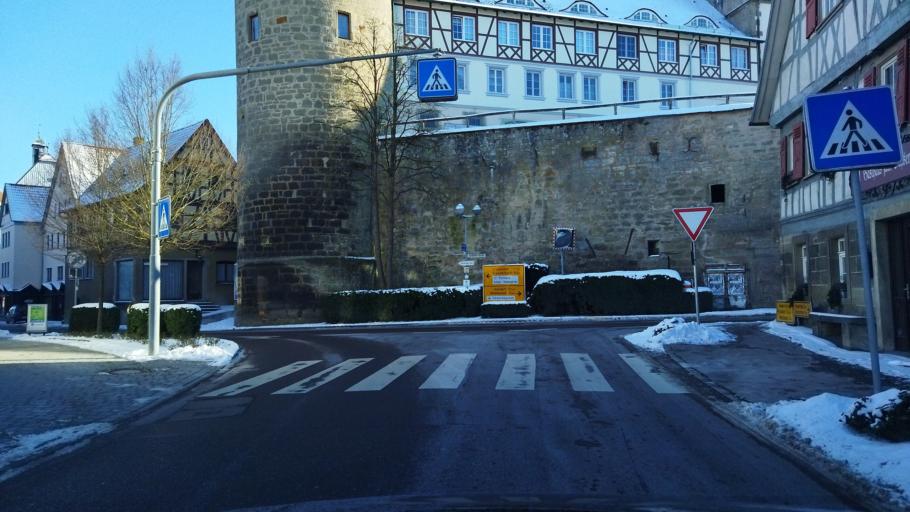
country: DE
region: Baden-Wuerttemberg
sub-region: Regierungsbezirk Stuttgart
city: Obersontheim
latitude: 49.0578
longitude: 9.8969
